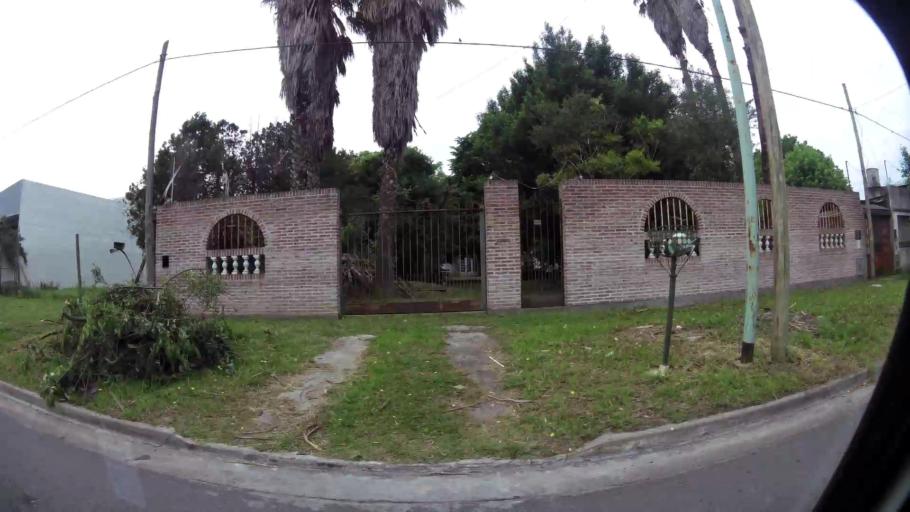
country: AR
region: Buenos Aires
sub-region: Partido de La Plata
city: La Plata
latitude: -34.9277
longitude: -58.0008
